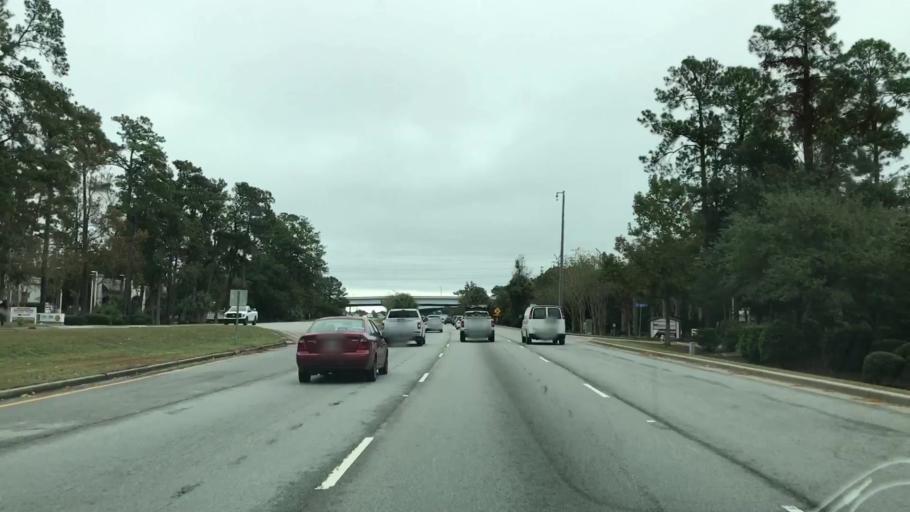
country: US
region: South Carolina
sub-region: Beaufort County
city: Bluffton
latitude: 32.2360
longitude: -80.8070
